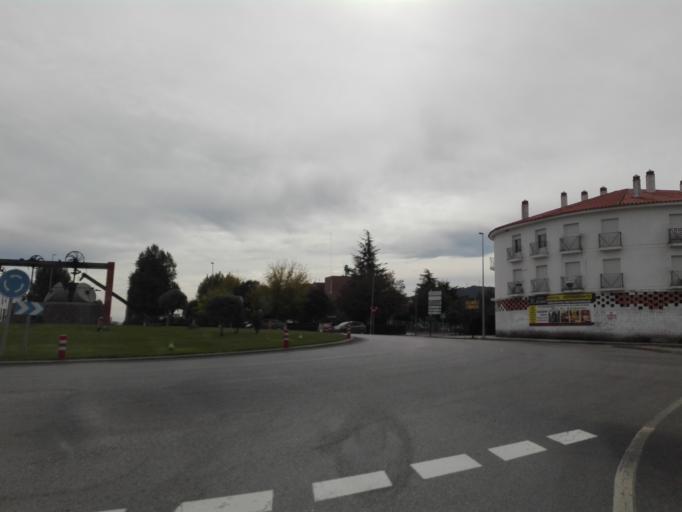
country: ES
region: Extremadura
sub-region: Provincia de Badajoz
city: Llerena
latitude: 38.2445
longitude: -6.0146
